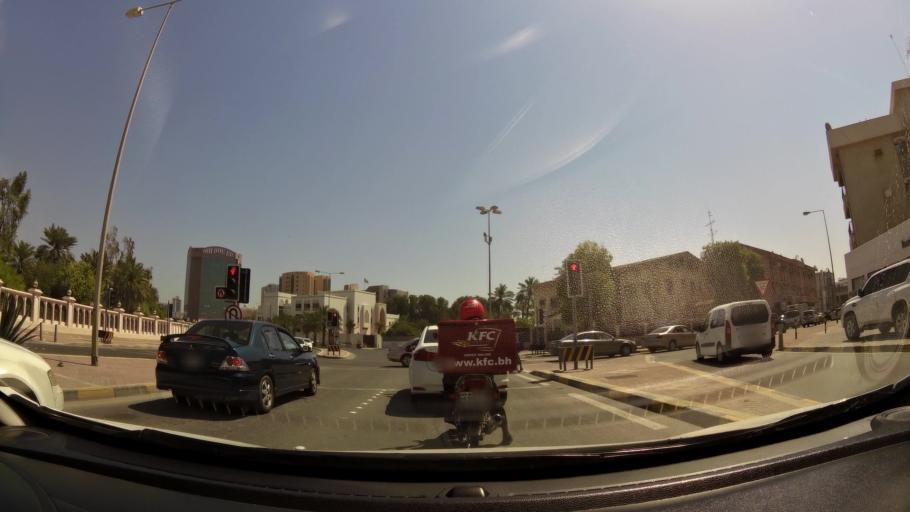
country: BH
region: Manama
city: Manama
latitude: 26.2169
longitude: 50.5912
